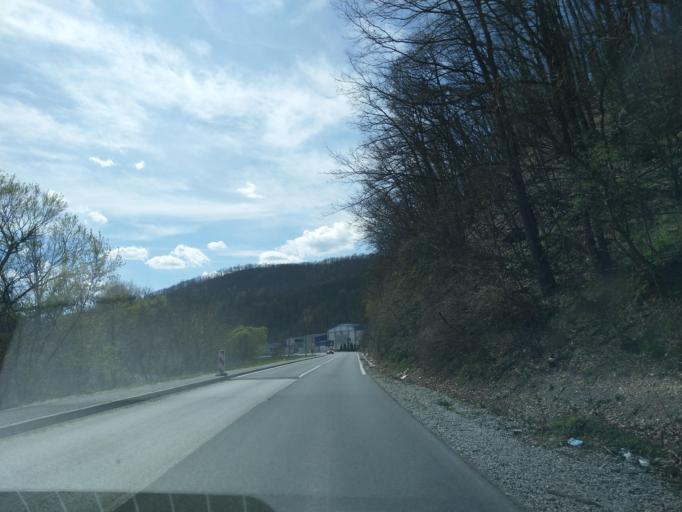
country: RS
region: Central Serbia
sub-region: Zlatiborski Okrug
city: Arilje
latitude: 43.7839
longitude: 20.1076
